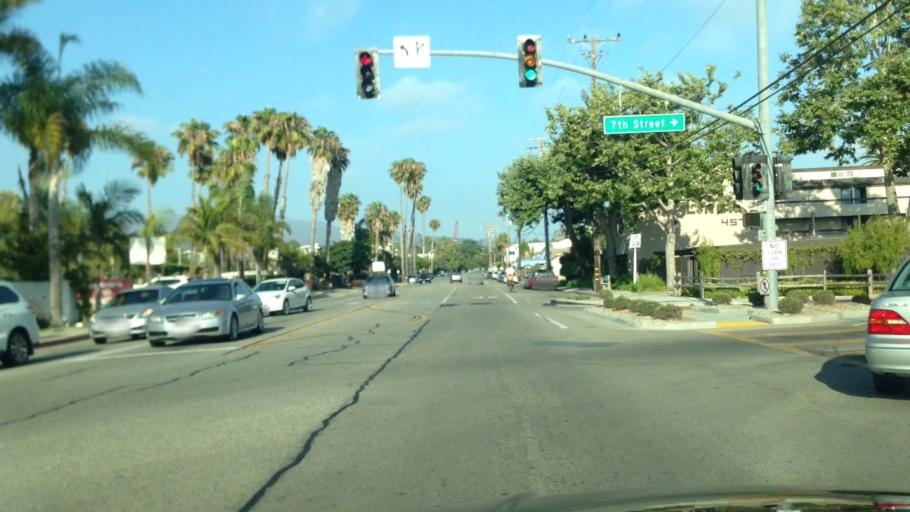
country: US
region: California
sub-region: Santa Barbara County
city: Carpinteria
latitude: 34.4018
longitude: -119.5265
